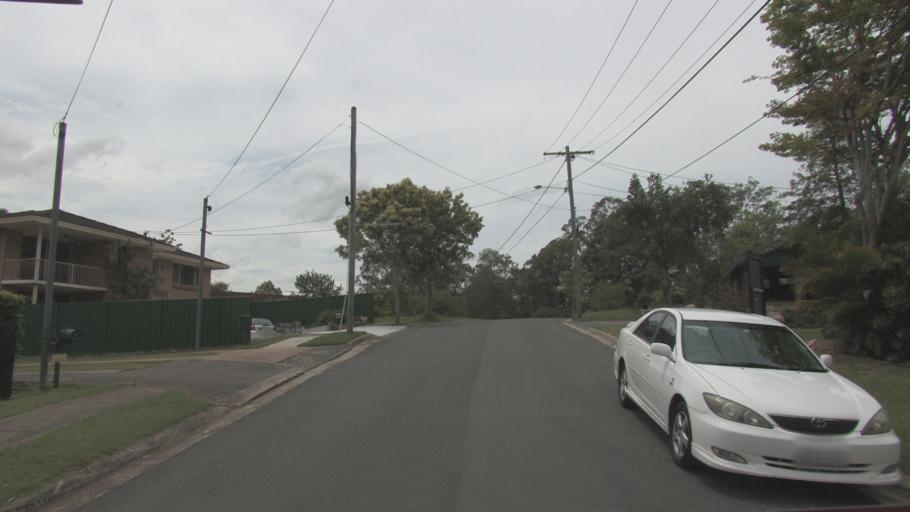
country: AU
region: Queensland
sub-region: Logan
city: Slacks Creek
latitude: -27.6569
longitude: 153.1603
